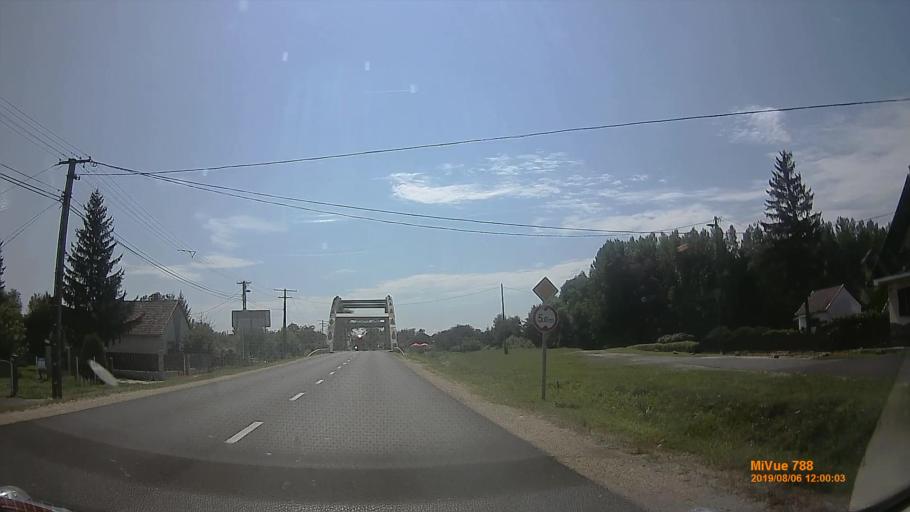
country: HU
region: Vas
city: Vasvar
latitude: 47.0645
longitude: 16.7450
